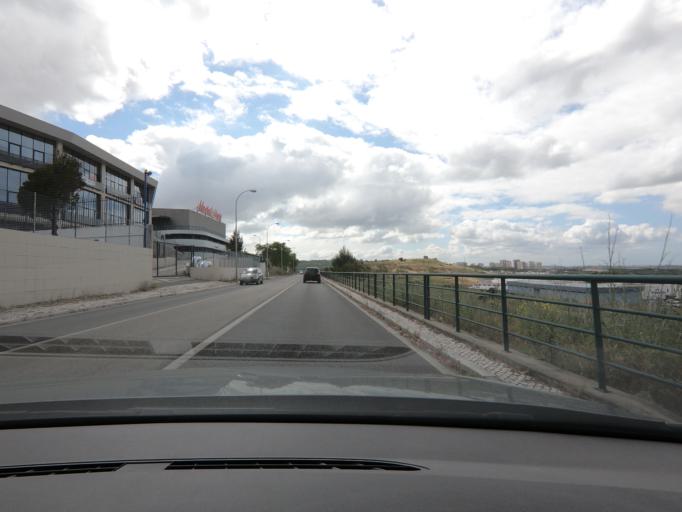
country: PT
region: Lisbon
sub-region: Oeiras
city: Carnaxide
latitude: 38.7292
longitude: -9.2242
